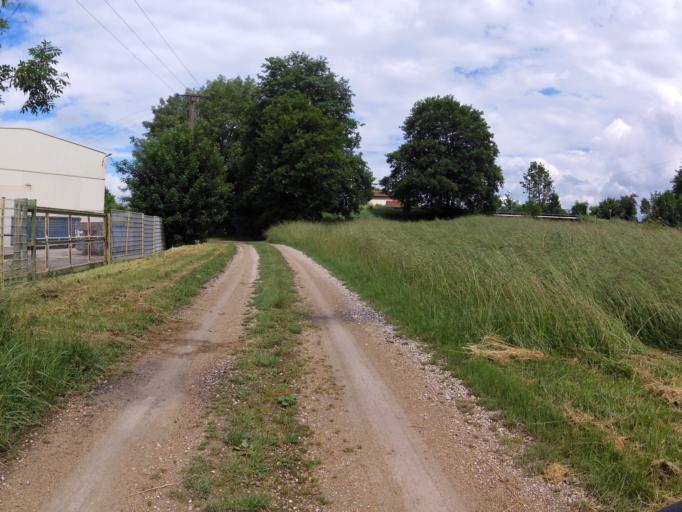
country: FR
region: Lorraine
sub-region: Departement de la Meuse
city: Revigny-sur-Ornain
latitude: 48.8082
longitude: 4.9584
